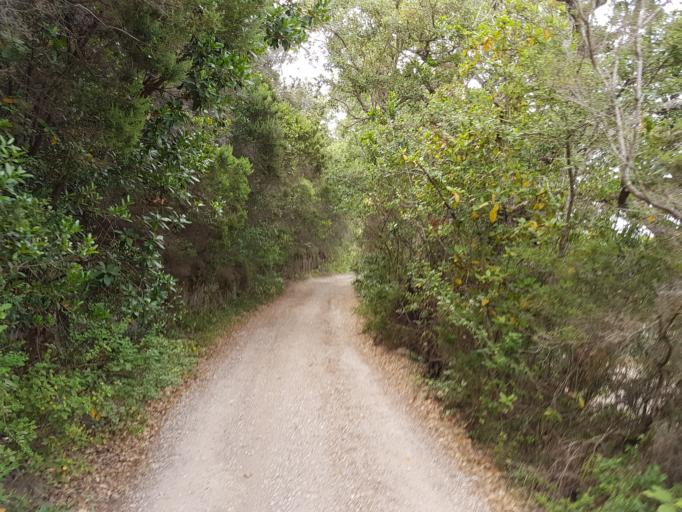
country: IT
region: Tuscany
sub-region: Provincia di Livorno
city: Portoferraio
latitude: 42.7857
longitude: 10.3497
